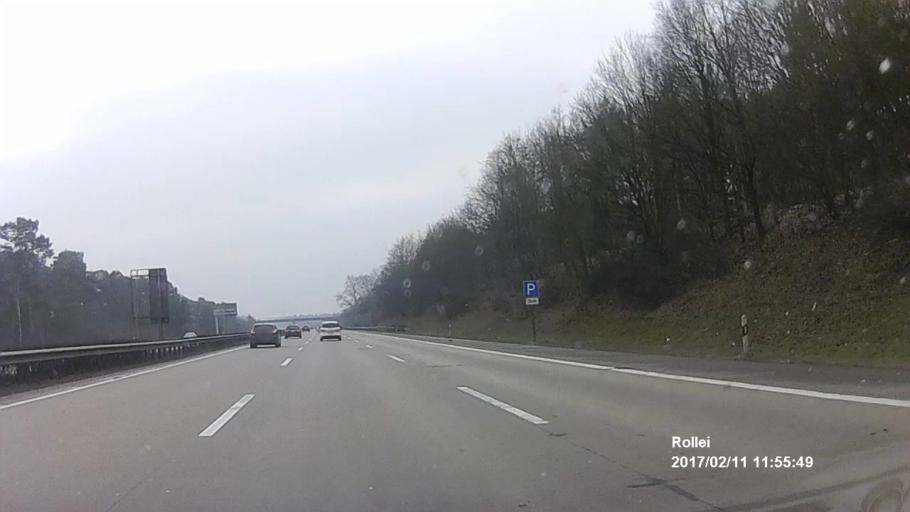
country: DE
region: Lower Saxony
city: Elze
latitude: 52.6005
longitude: 9.7461
